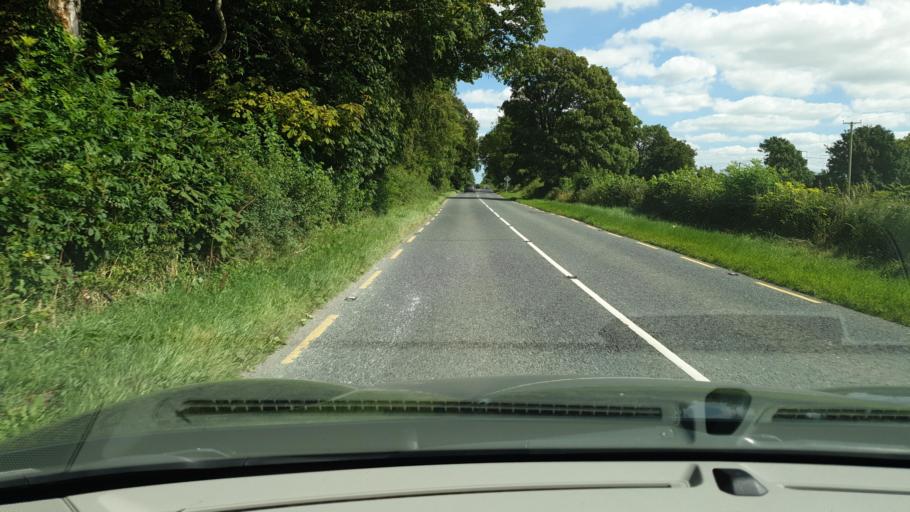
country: IE
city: Confey
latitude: 53.4369
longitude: -6.5254
